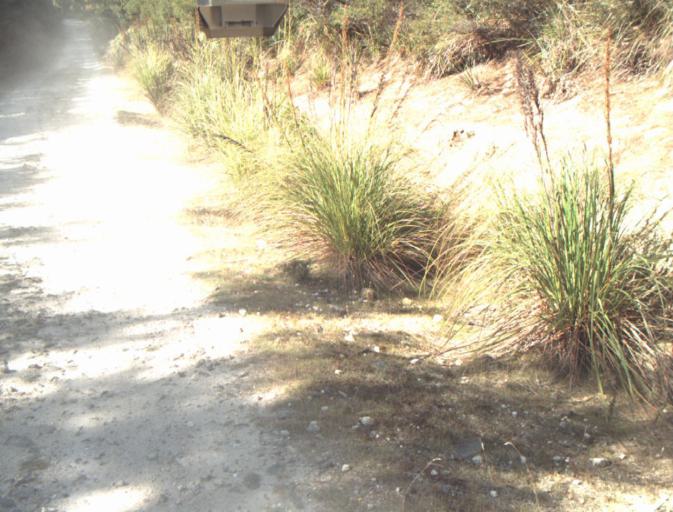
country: AU
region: Tasmania
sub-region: Dorset
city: Bridport
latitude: -41.1518
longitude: 147.2040
